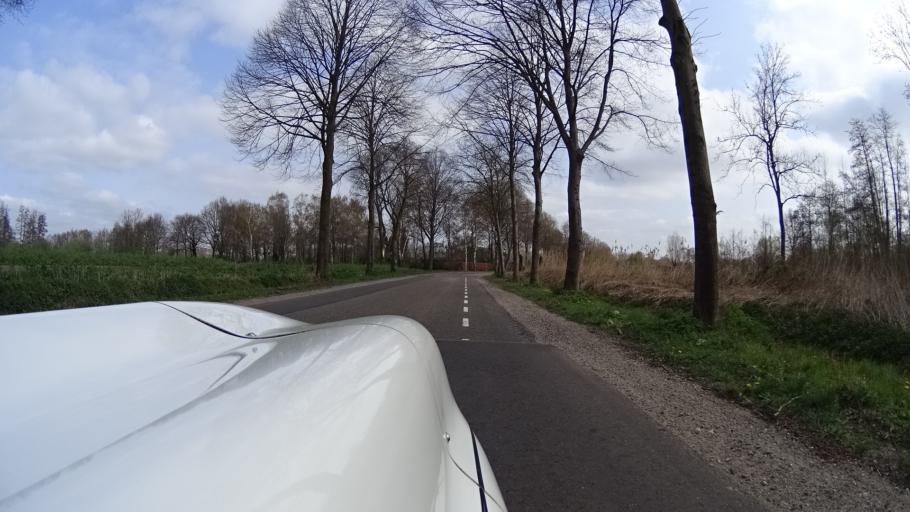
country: NL
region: North Brabant
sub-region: Gemeente Veghel
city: Keldonk
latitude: 51.5893
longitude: 5.5977
